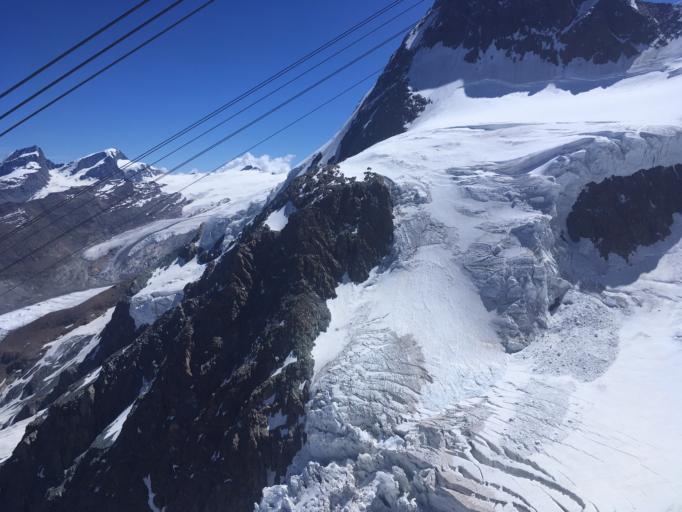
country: CH
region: Valais
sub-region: Visp District
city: Zermatt
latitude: 45.9423
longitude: 7.7264
